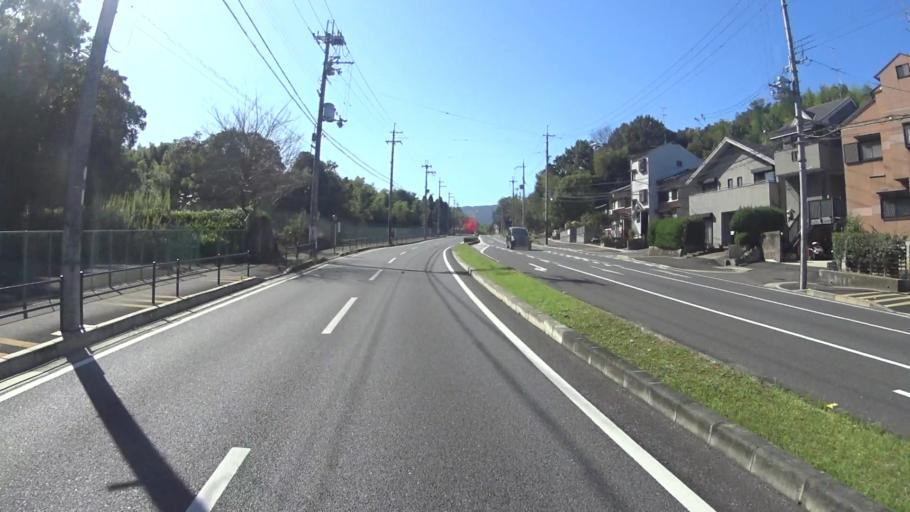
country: JP
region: Kyoto
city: Muko
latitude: 34.9641
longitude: 135.6863
